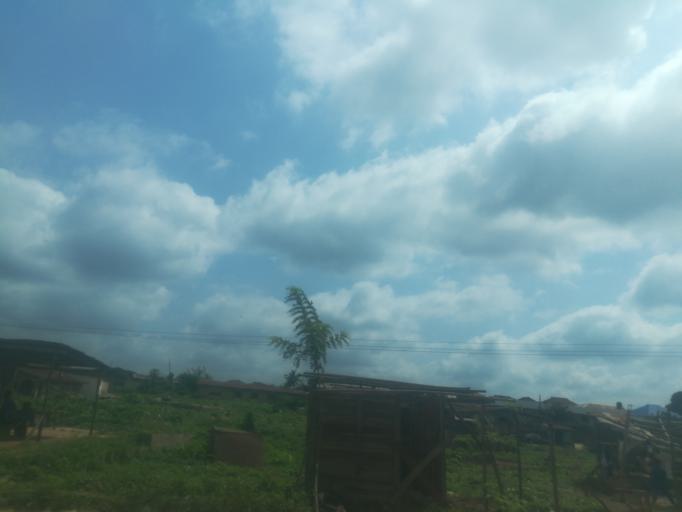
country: NG
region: Oyo
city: Moniya
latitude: 7.5344
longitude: 3.9118
